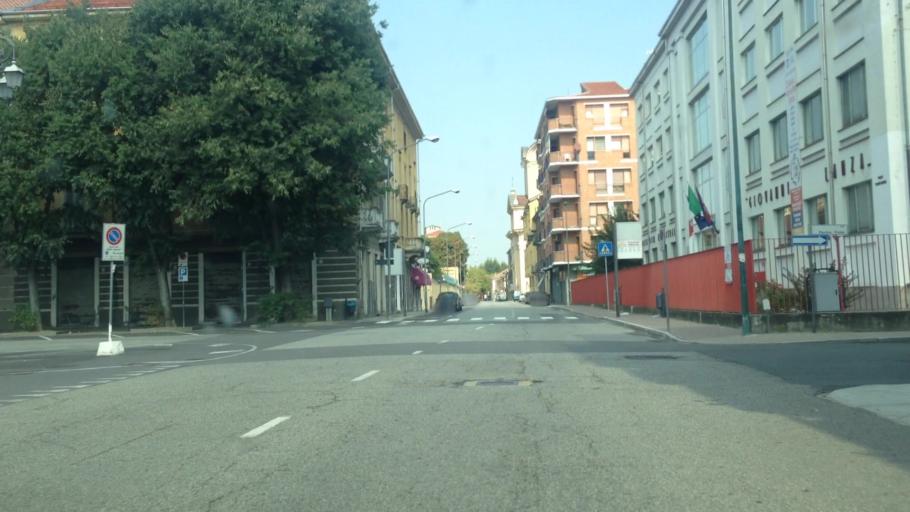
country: IT
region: Piedmont
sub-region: Provincia di Alessandria
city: Casale Monferrato
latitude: 45.1359
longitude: 8.4562
